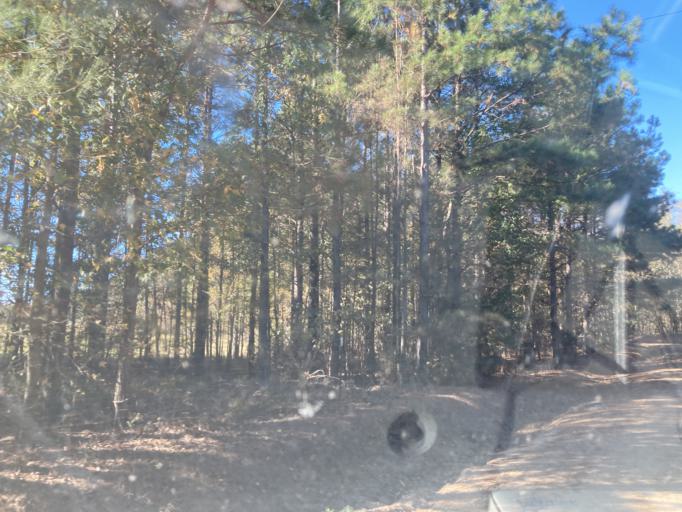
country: US
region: Mississippi
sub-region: Madison County
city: Kearney Park
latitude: 32.6717
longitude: -90.3406
